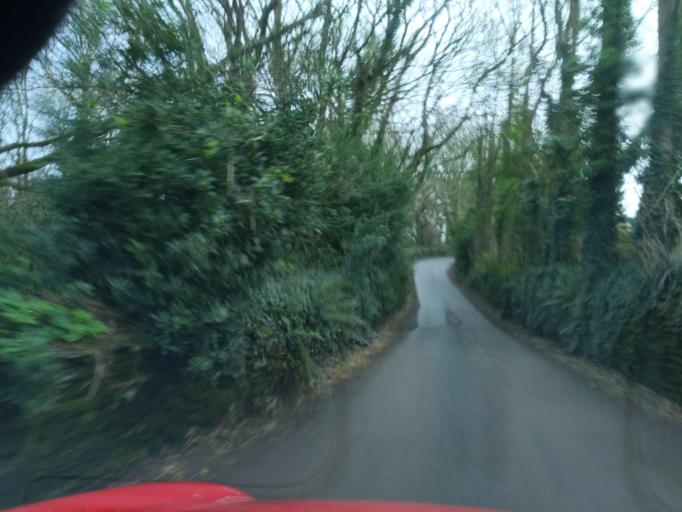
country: GB
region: England
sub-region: Devon
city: Wembury
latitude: 50.3285
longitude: -4.0902
